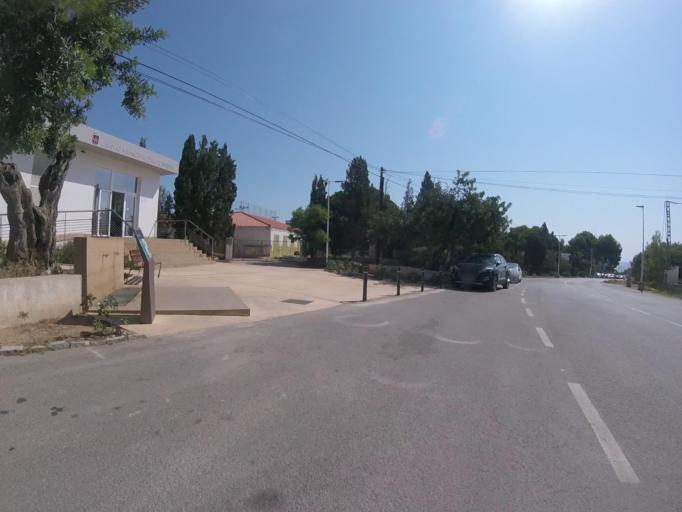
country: ES
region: Valencia
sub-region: Provincia de Castello
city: Alcoceber
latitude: 40.2500
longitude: 0.2835
